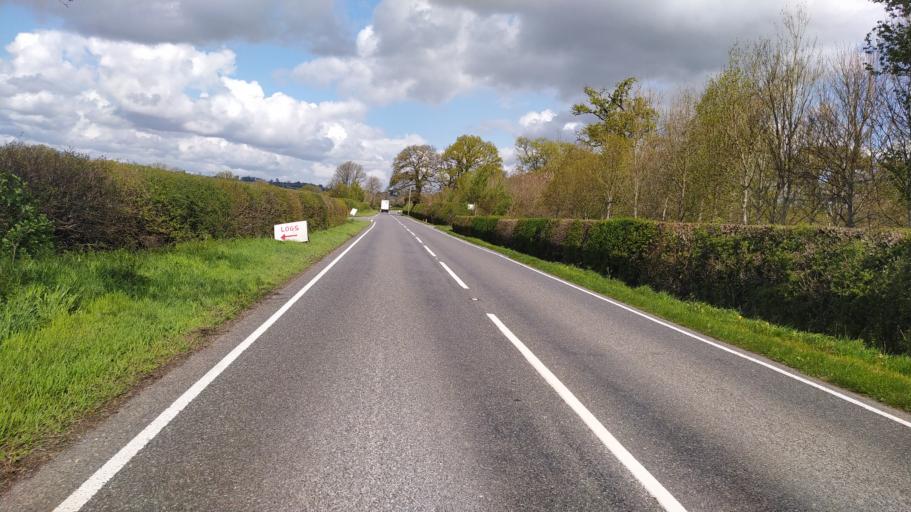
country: GB
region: England
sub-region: Somerset
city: Frome
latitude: 51.1844
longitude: -2.3141
